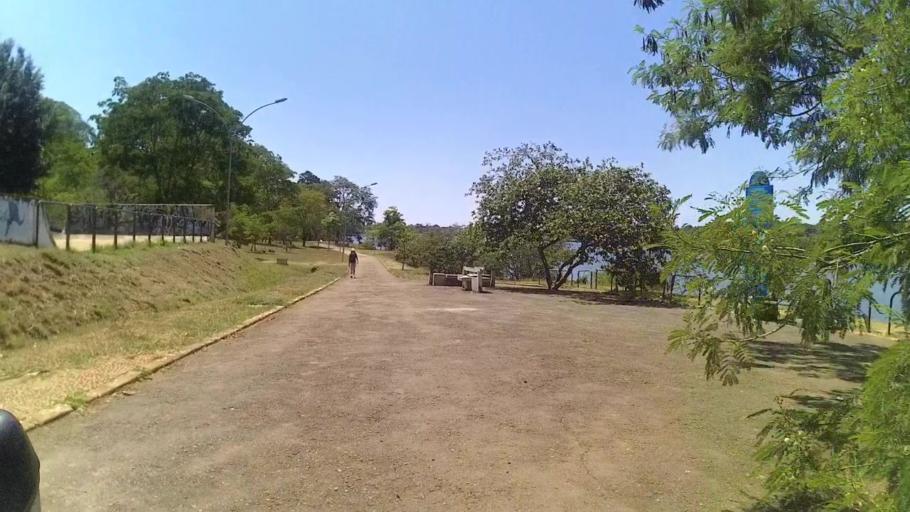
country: BR
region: Federal District
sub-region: Brasilia
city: Brasilia
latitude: -15.7295
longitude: -47.8924
